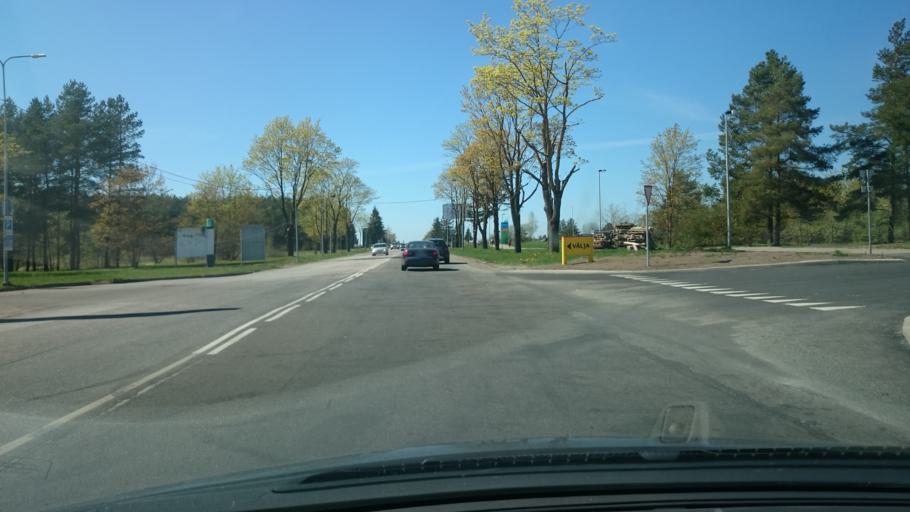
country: EE
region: Ida-Virumaa
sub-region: Narva linn
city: Narva
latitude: 59.3846
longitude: 28.1576
